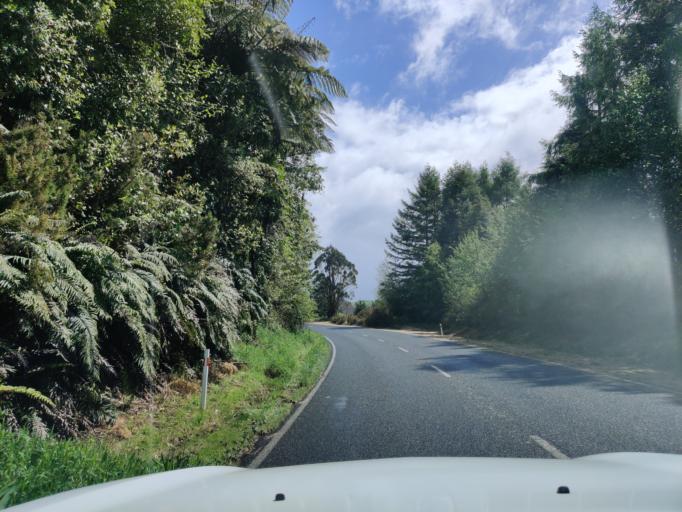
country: NZ
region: Bay of Plenty
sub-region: Rotorua District
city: Rotorua
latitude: -38.1765
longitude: 176.3260
